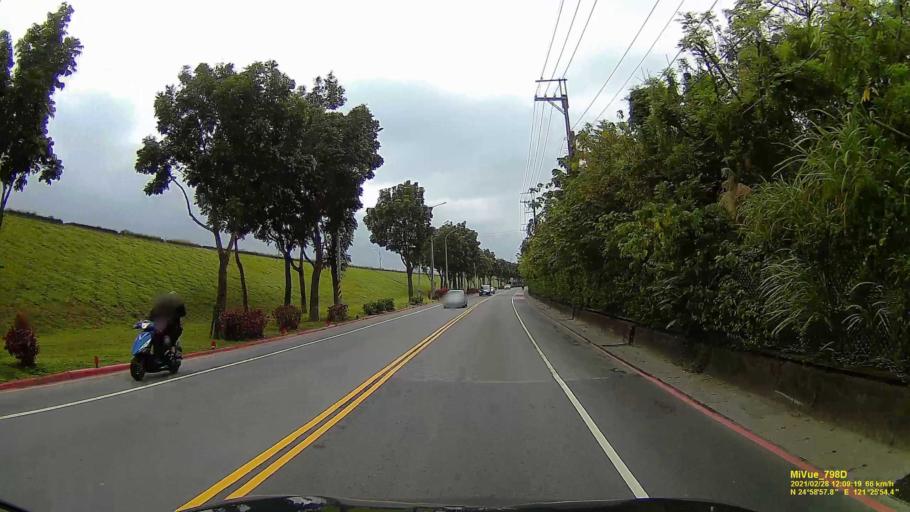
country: TW
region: Taipei
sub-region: Taipei
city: Banqiao
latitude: 24.9825
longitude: 121.4316
